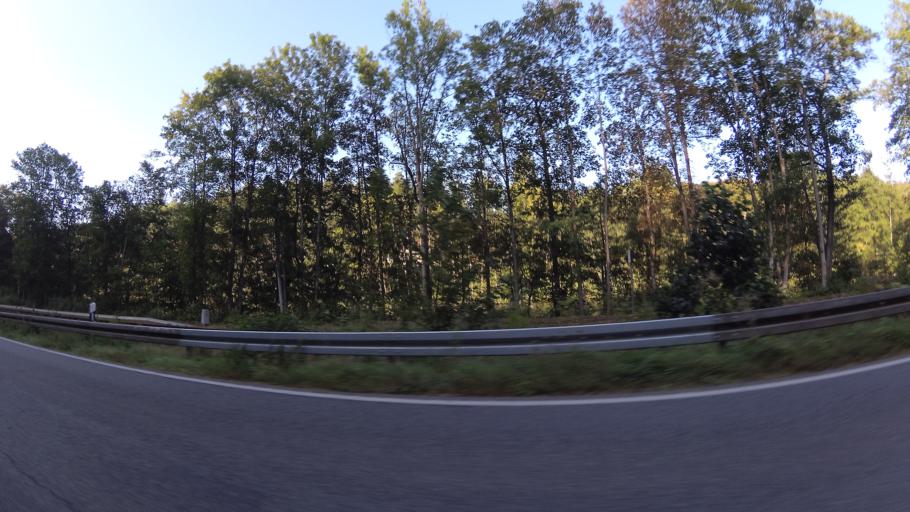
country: DE
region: Saarland
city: Kirkel
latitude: 49.2470
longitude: 7.1841
